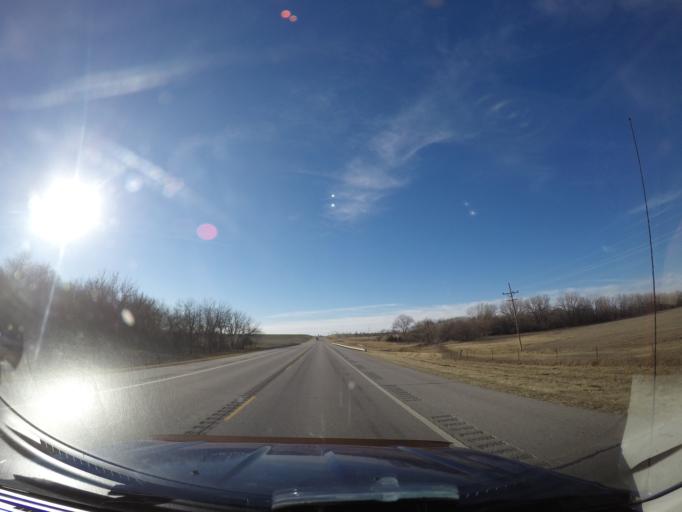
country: US
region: Kansas
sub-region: Marion County
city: Hillsboro
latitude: 38.3624
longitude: -97.3230
